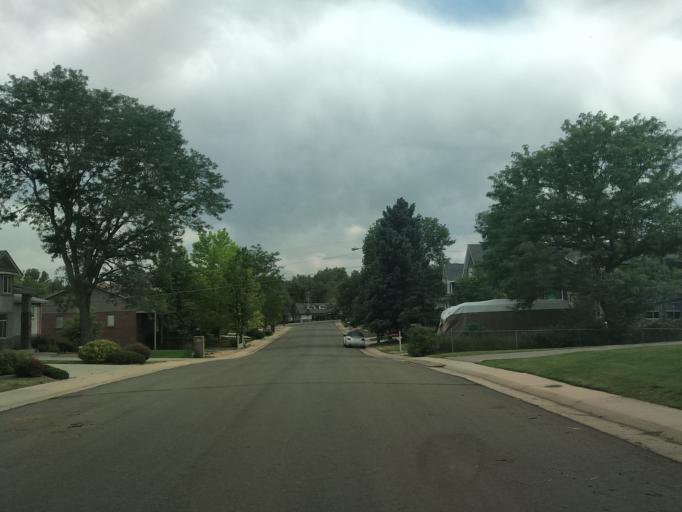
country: US
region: Colorado
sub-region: Jefferson County
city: Lakewood
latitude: 39.7022
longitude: -105.0922
